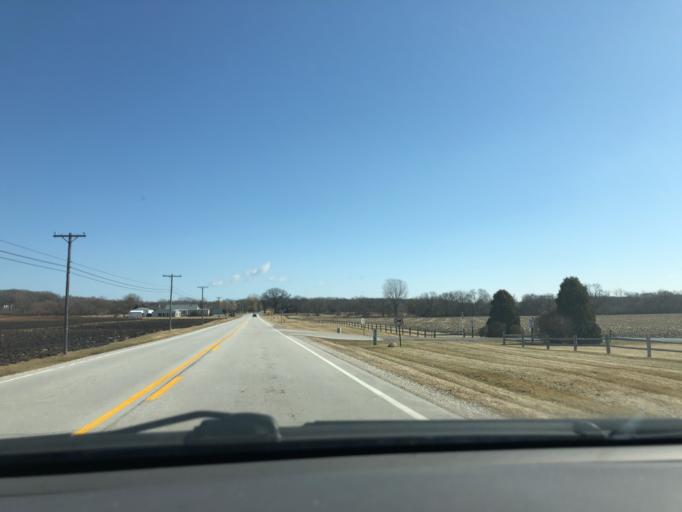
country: US
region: Illinois
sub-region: Kane County
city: Hampshire
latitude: 42.1065
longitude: -88.5154
